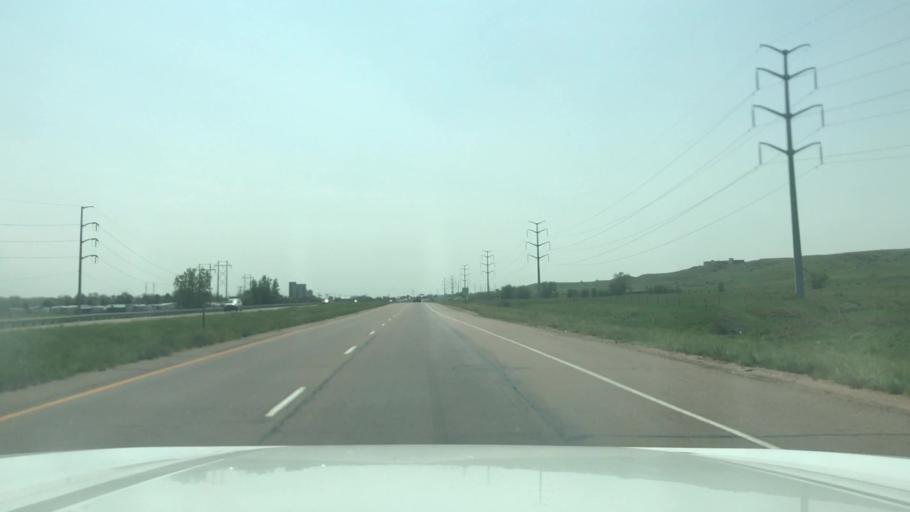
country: US
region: Colorado
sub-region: El Paso County
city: Security-Widefield
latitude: 38.7181
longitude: -104.7282
